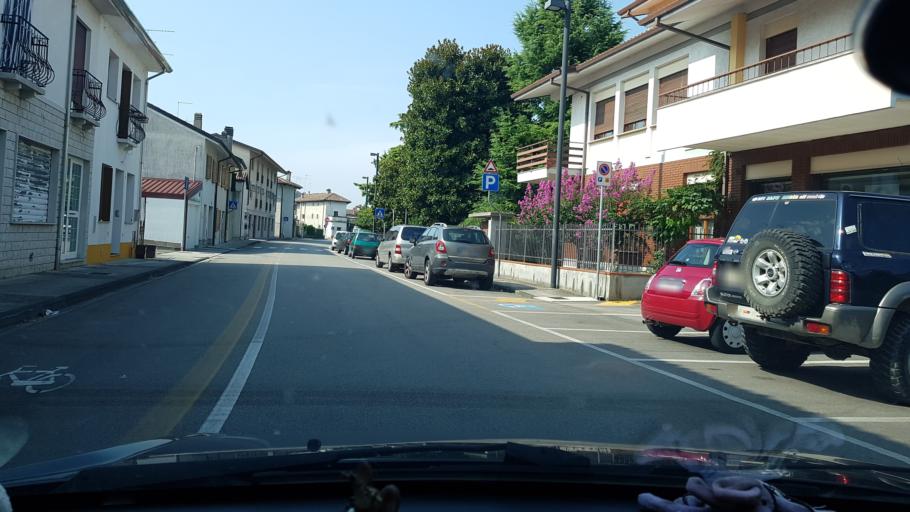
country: IT
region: Friuli Venezia Giulia
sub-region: Provincia di Gorizia
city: Fogliano
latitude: 45.8658
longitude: 13.4810
